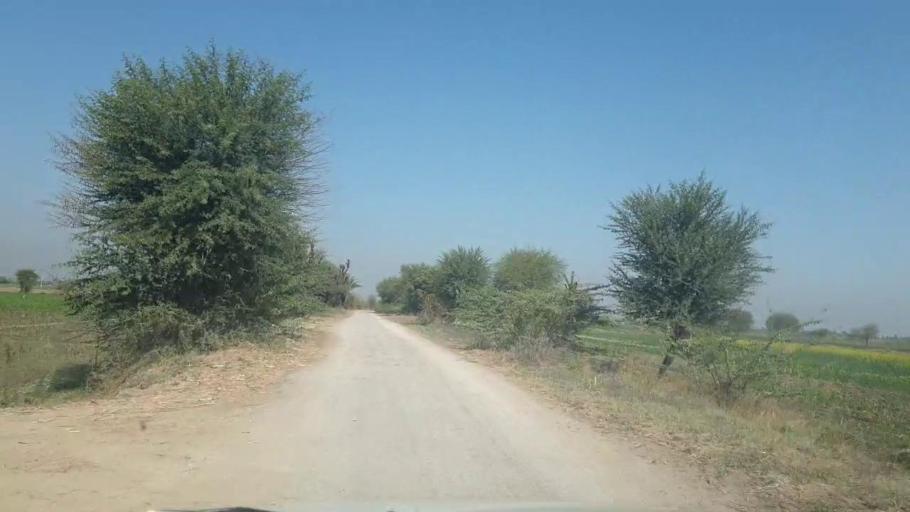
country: PK
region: Sindh
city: Mirpur Khas
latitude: 25.5057
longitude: 69.1719
